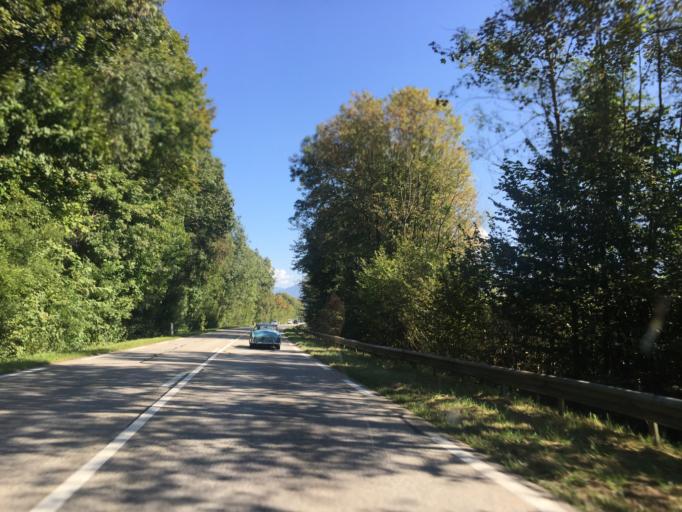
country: FR
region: Rhone-Alpes
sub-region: Departement de la Savoie
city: Gresy-sur-Isere
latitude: 45.6082
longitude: 6.2842
